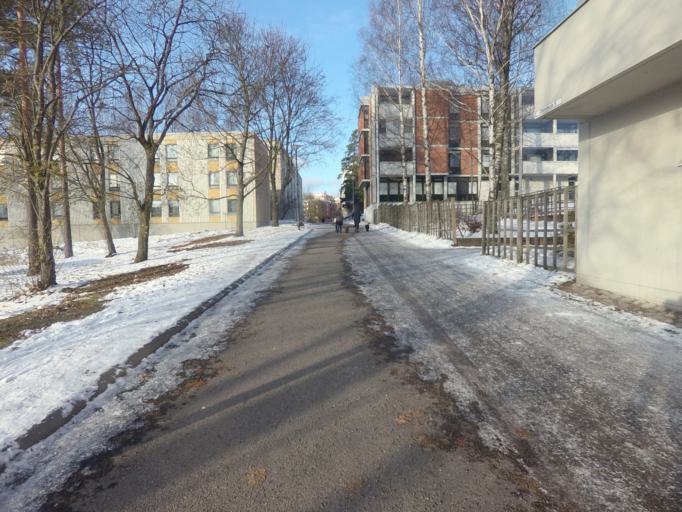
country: FI
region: Uusimaa
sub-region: Helsinki
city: Koukkuniemi
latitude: 60.1691
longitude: 24.7289
